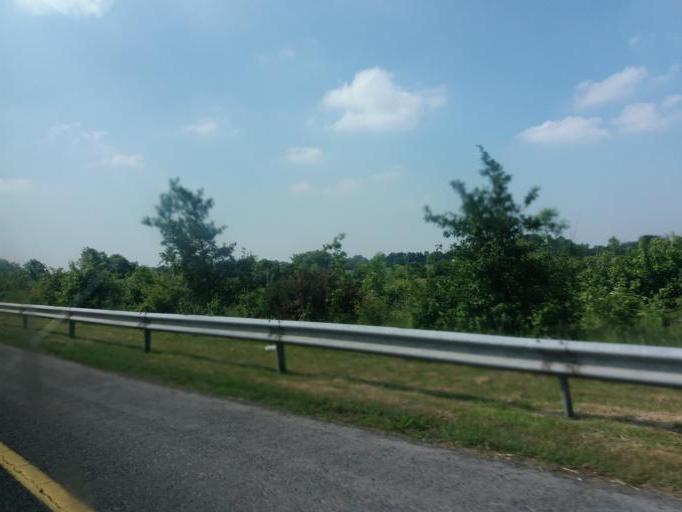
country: IE
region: Leinster
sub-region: An Mhi
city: Ashbourne
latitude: 53.5023
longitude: -6.4186
